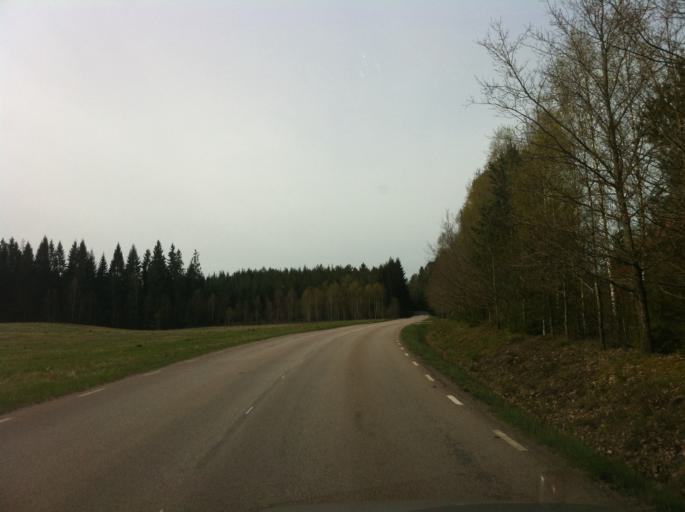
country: SE
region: Vaestra Goetaland
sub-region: Bollebygds Kommun
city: Bollebygd
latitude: 57.7163
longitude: 12.5855
